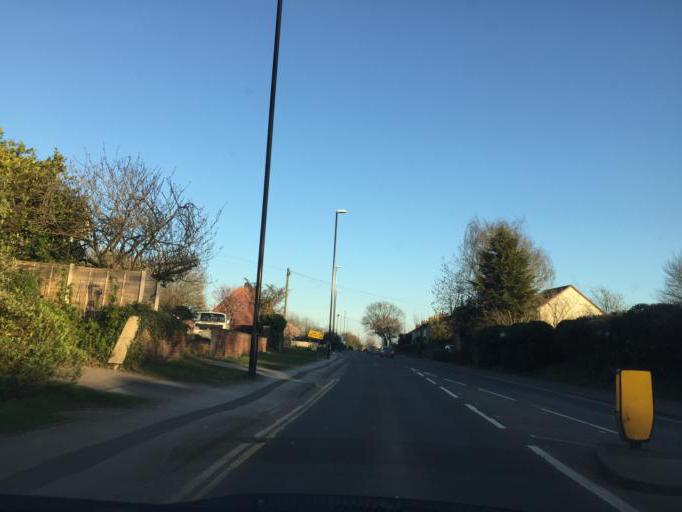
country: GB
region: England
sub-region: Warwickshire
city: Ryton on Dunsmore
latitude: 52.4011
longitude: -1.4448
